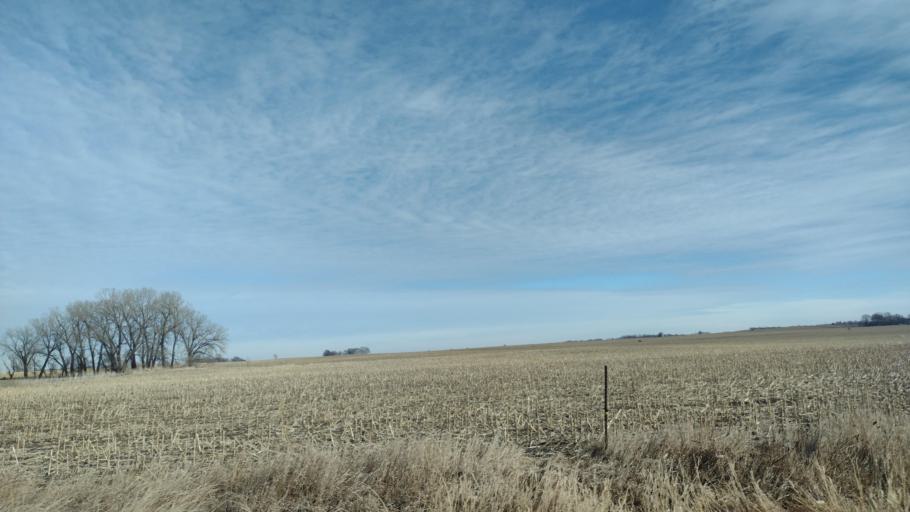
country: US
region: South Dakota
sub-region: Union County
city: Beresford
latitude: 42.9456
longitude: -96.8054
